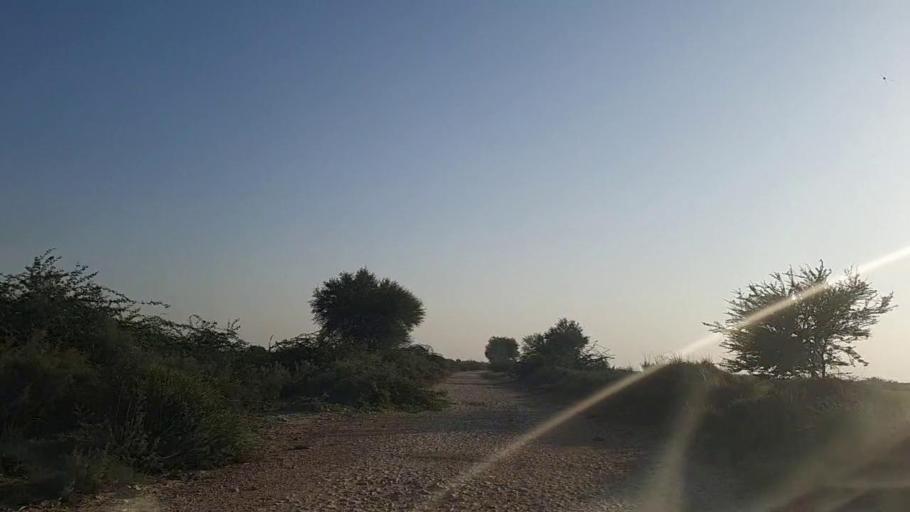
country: PK
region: Sindh
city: Jati
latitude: 24.4318
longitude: 68.1911
